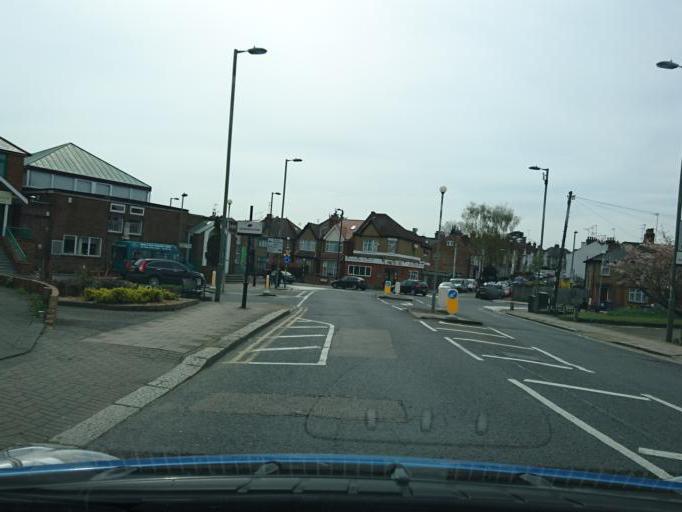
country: GB
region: England
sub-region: Greater London
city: Hadley Wood
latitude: 51.6438
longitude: -0.1656
